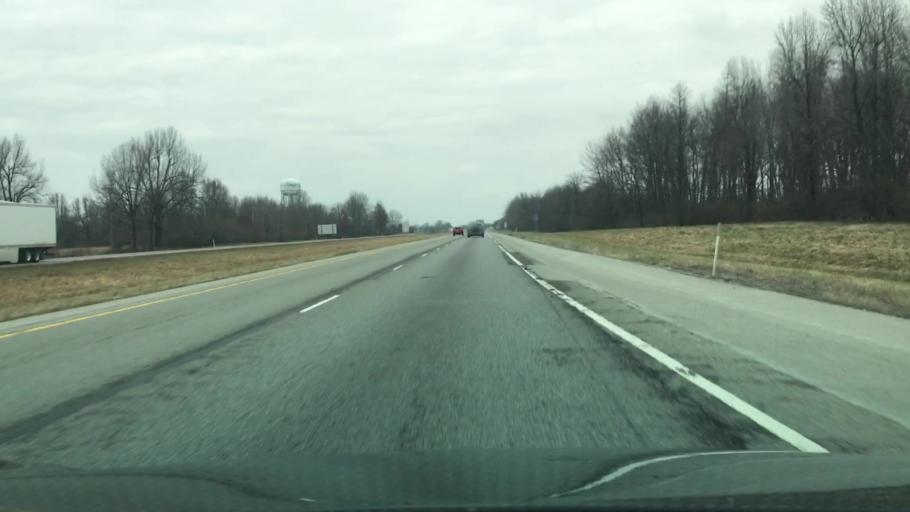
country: US
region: Illinois
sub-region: Massac County
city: Metropolis
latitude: 37.1673
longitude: -88.6824
